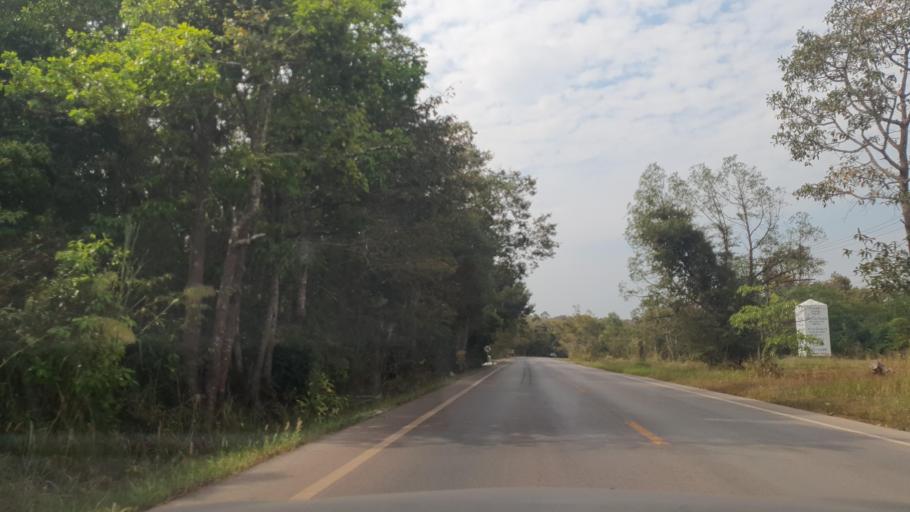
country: TH
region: Changwat Bueng Kan
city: Bung Khla
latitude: 18.2873
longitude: 103.8989
